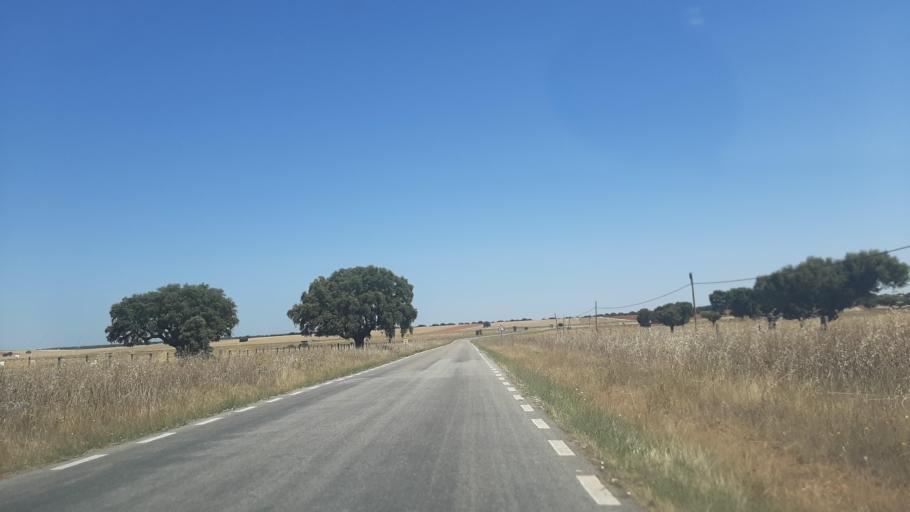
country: ES
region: Castille and Leon
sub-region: Provincia de Salamanca
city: Cabrillas
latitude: 40.7130
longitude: -6.1786
